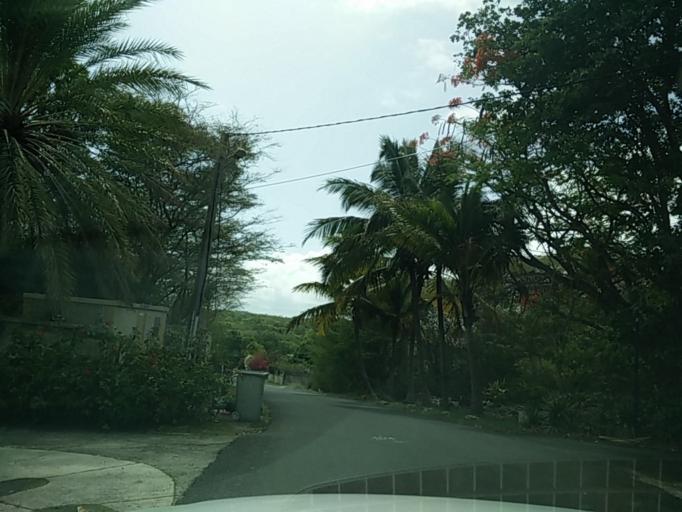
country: GP
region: Guadeloupe
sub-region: Guadeloupe
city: Sainte-Anne
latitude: 16.2193
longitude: -61.4035
